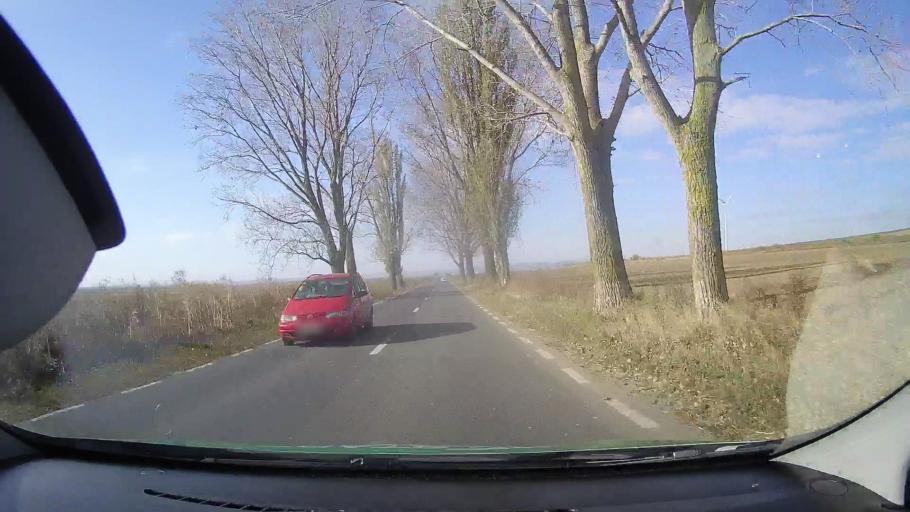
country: RO
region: Tulcea
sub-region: Comuna Valea Nucarilor
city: Iazurile
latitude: 45.0241
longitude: 28.9729
